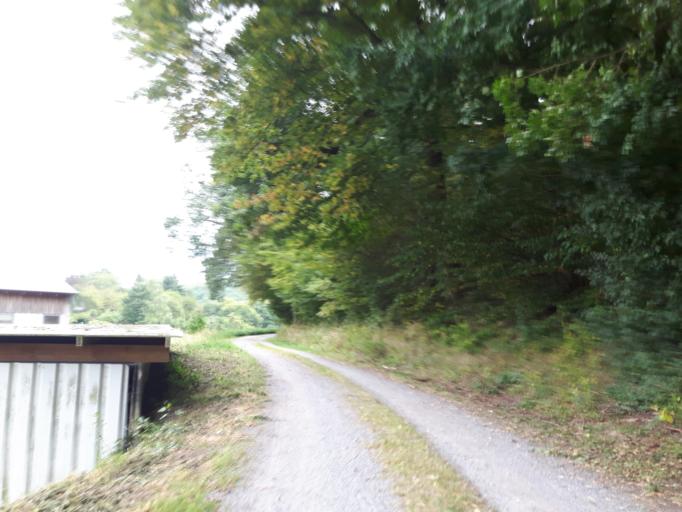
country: DE
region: Baden-Wuerttemberg
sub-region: Karlsruhe Region
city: Sternenfels
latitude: 49.0514
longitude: 8.8589
